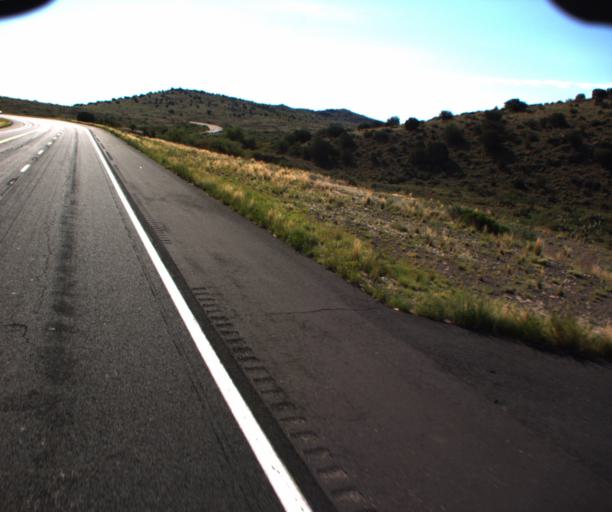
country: US
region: Arizona
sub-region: Greenlee County
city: Clifton
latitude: 32.8513
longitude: -109.3166
